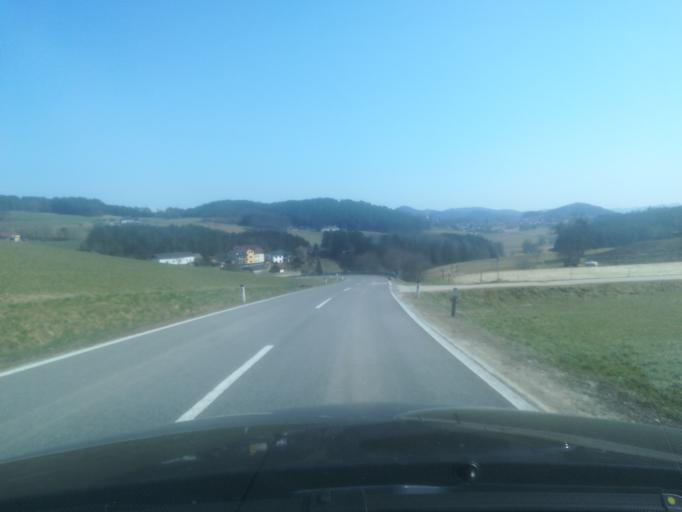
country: AT
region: Upper Austria
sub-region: Politischer Bezirk Freistadt
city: Freistadt
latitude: 48.4310
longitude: 14.5850
